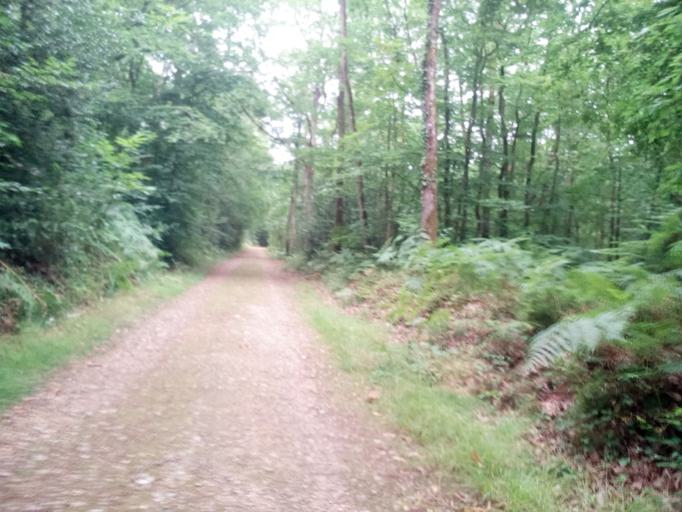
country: FR
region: Lower Normandy
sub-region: Departement du Calvados
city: Clinchamps-sur-Orne
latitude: 49.0412
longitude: -0.4372
